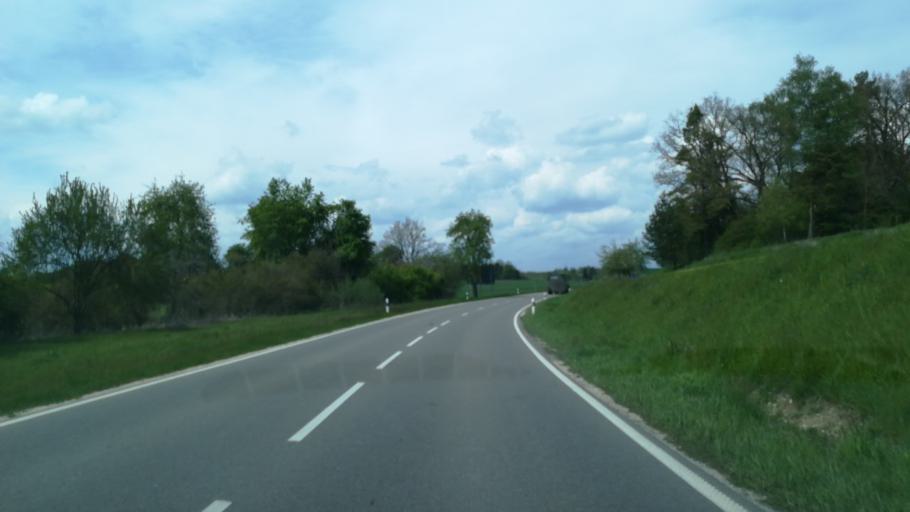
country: DE
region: Baden-Wuerttemberg
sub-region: Tuebingen Region
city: Messkirch
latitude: 48.0061
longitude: 9.1149
